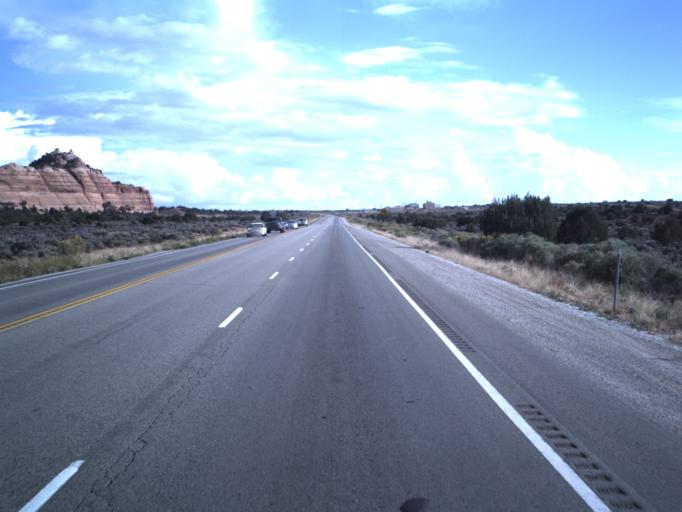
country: US
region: Utah
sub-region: Grand County
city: Moab
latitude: 38.3399
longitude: -109.4329
